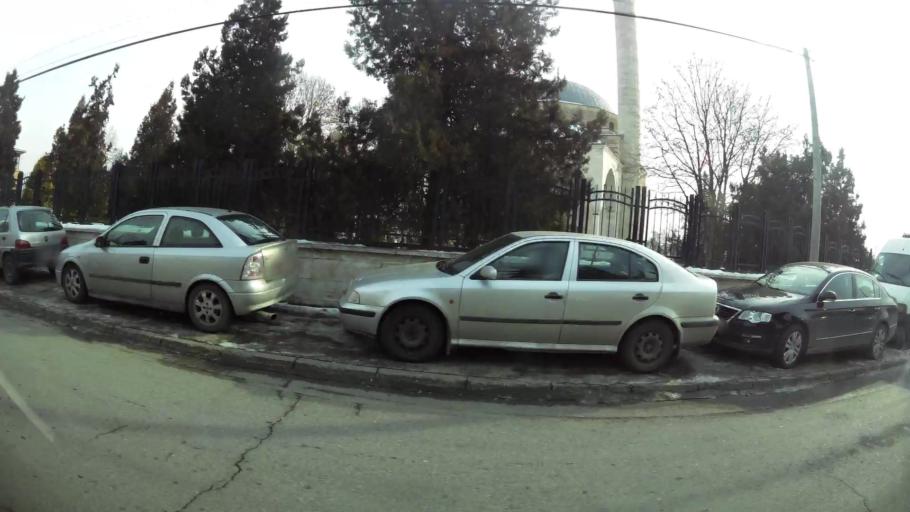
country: MK
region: Karpos
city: Skopje
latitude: 42.0023
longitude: 21.4349
